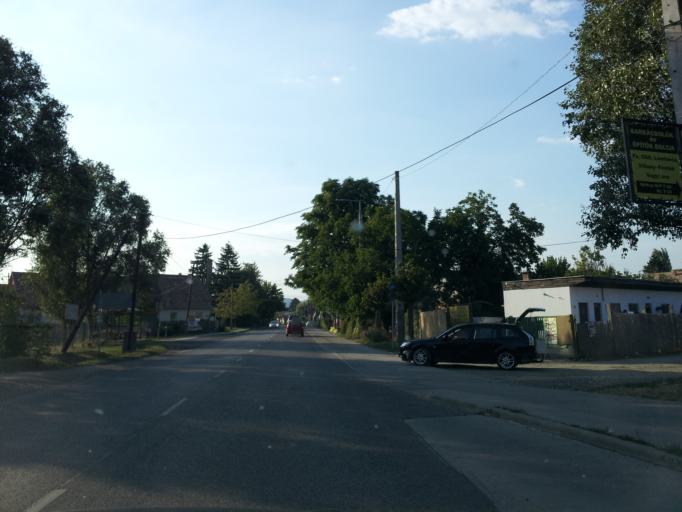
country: HU
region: Pest
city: Dunabogdany
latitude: 47.7894
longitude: 19.0415
